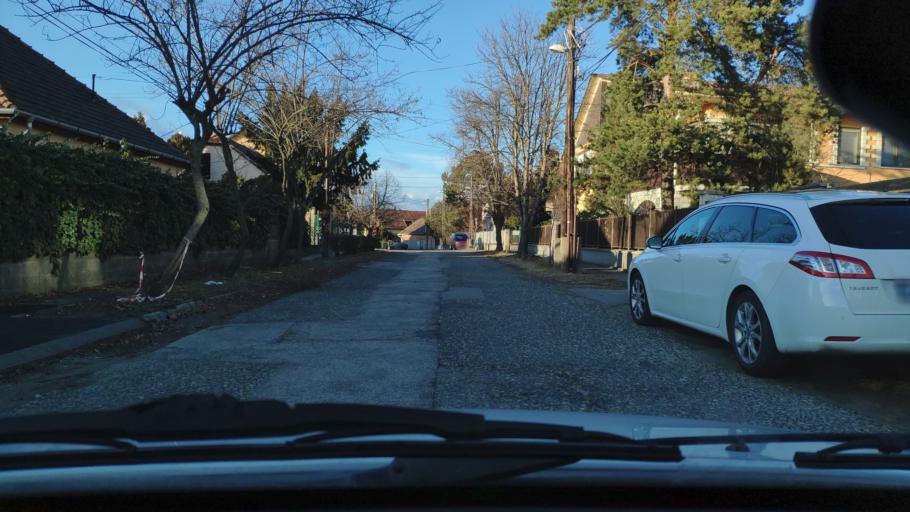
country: HU
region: Budapest
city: Budapest XXIII. keruelet
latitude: 47.4002
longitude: 19.0925
